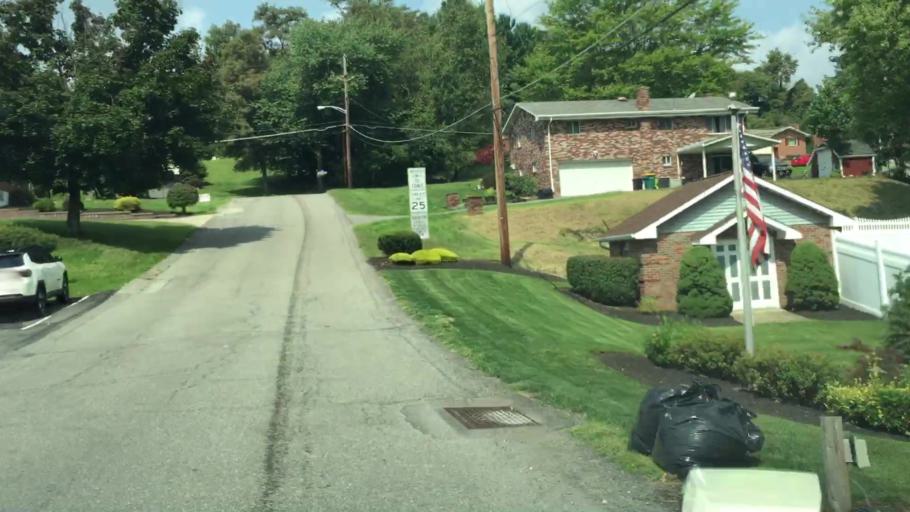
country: US
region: Pennsylvania
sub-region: Allegheny County
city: Coraopolis
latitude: 40.4703
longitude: -80.1365
